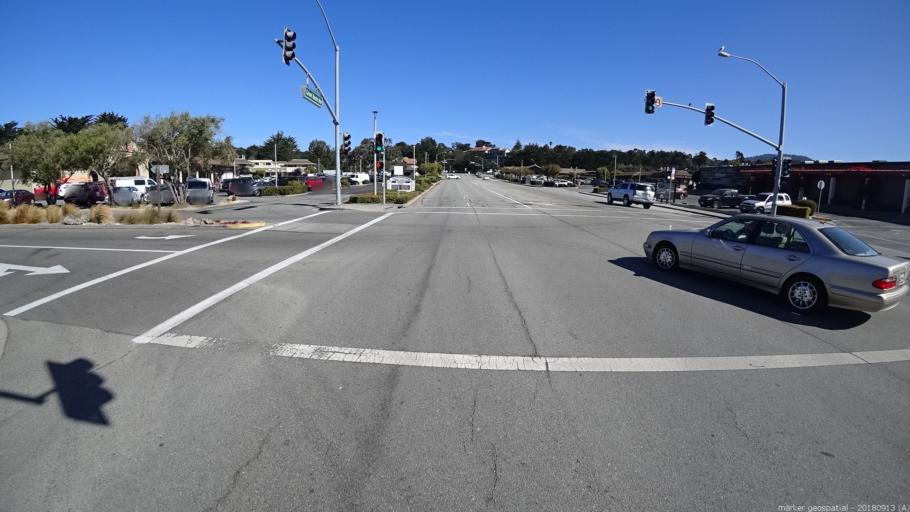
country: US
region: California
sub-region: Monterey County
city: Carmel-by-the-Sea
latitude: 36.5421
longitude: -121.9049
